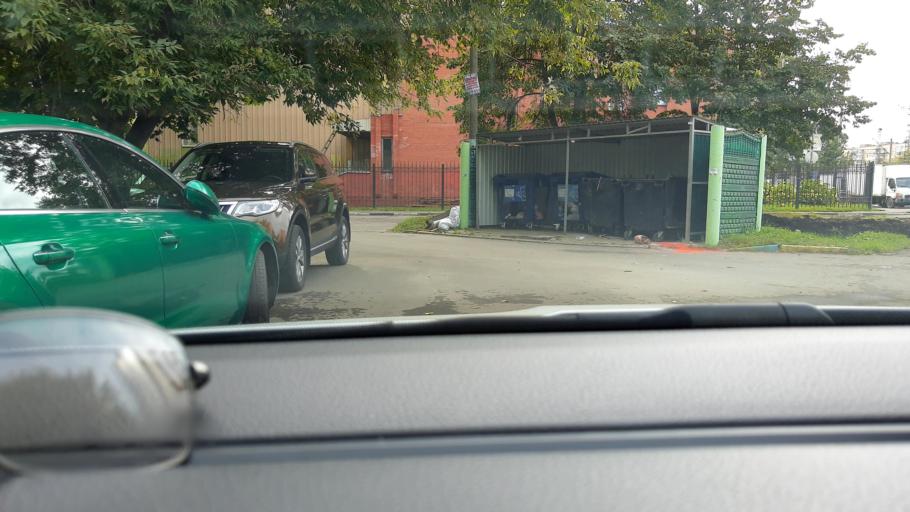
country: RU
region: Moskovskaya
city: Pavshino
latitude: 55.8152
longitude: 37.3469
